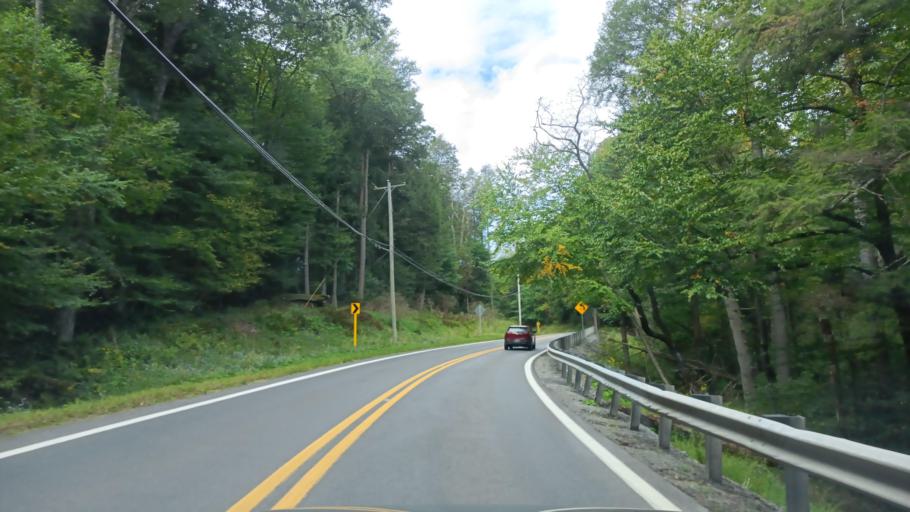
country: US
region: West Virginia
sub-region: Preston County
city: Terra Alta
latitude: 39.3248
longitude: -79.5406
